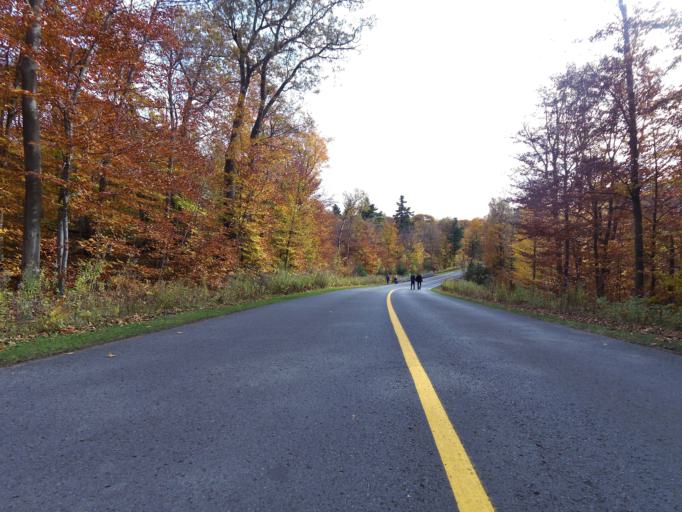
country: CA
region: Quebec
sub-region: Outaouais
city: Gatineau
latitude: 45.4806
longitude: -75.8441
